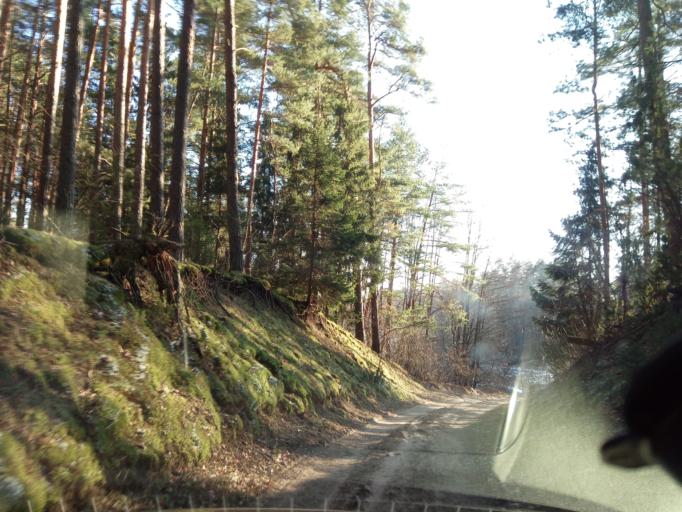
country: LT
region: Alytaus apskritis
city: Druskininkai
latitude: 53.9530
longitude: 23.8662
